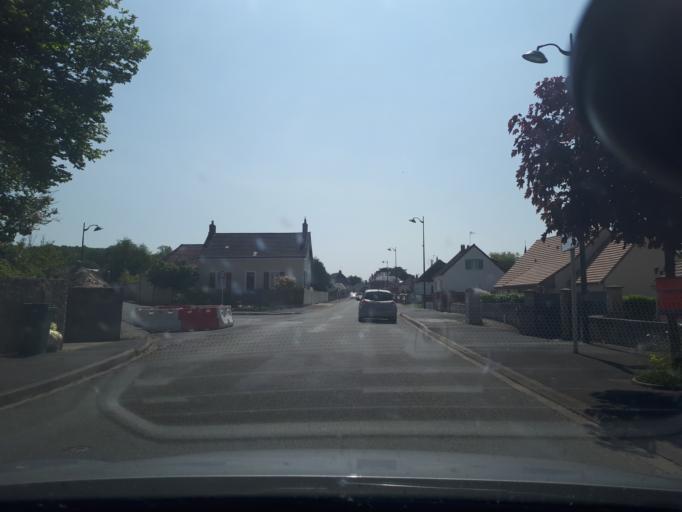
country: FR
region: Pays de la Loire
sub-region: Departement de la Sarthe
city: Le Breil-sur-Merize
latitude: 48.0110
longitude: 0.4741
